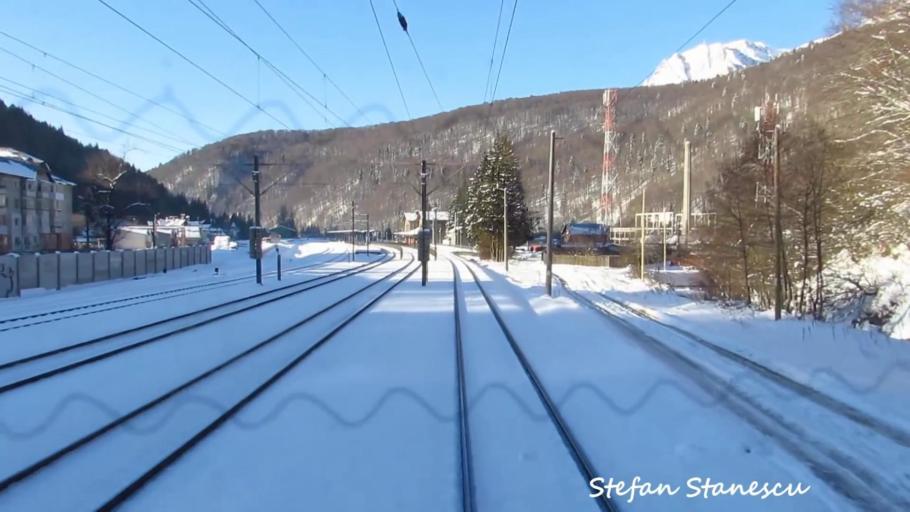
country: RO
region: Prahova
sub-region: Oras Azuga
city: Azuga
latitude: 45.4464
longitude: 25.5539
